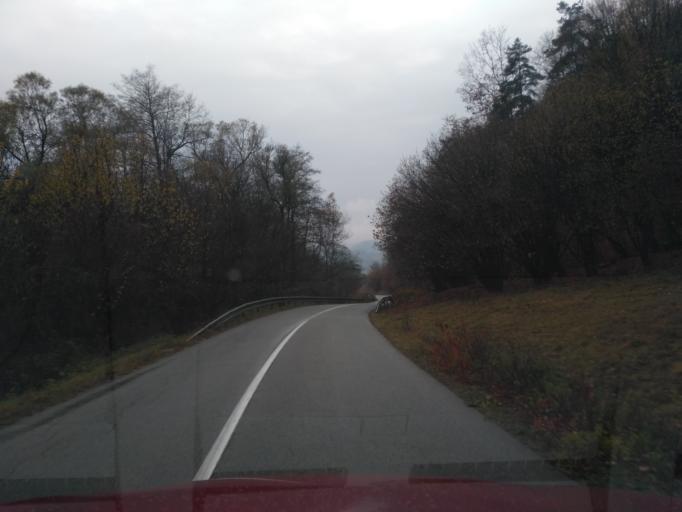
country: SK
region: Kosicky
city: Medzev
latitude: 48.7078
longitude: 20.8068
